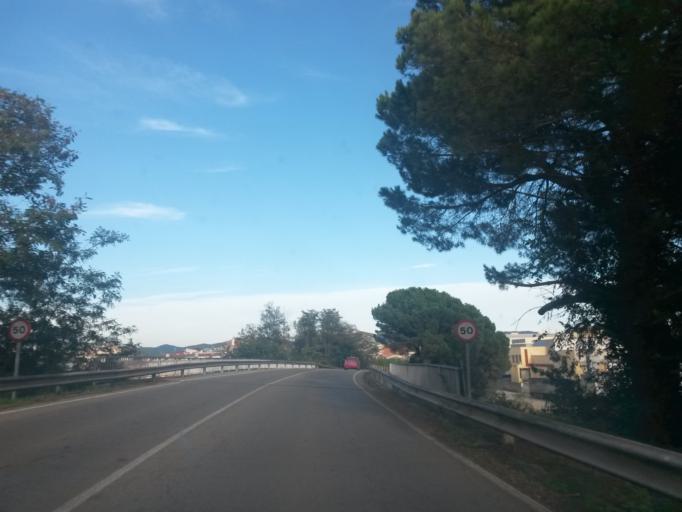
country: ES
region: Catalonia
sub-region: Provincia de Girona
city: Vilablareix
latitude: 41.9717
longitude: 2.7777
